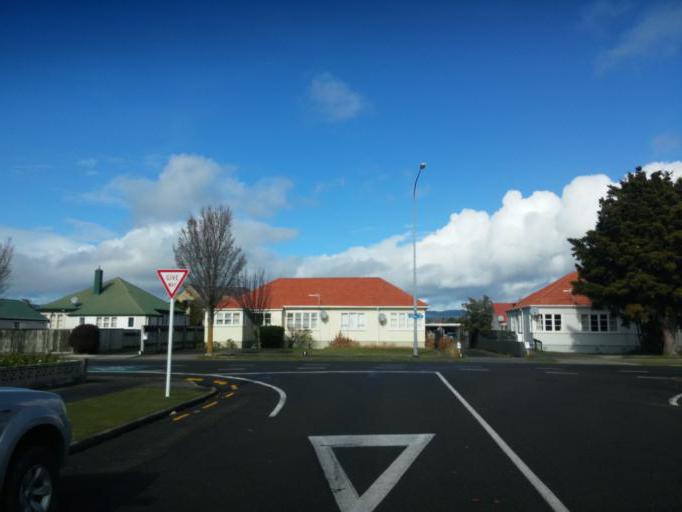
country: NZ
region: Manawatu-Wanganui
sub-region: Palmerston North City
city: Palmerston North
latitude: -40.3598
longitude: 175.6205
